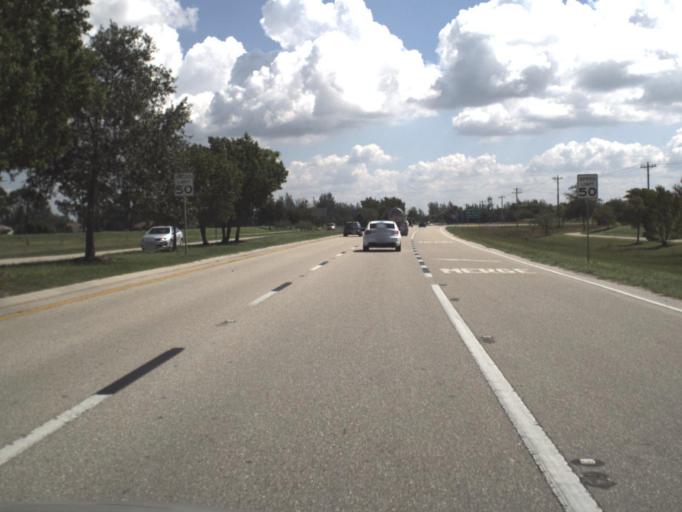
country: US
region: Florida
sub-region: Lee County
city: Cape Coral
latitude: 26.6072
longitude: -82.0224
